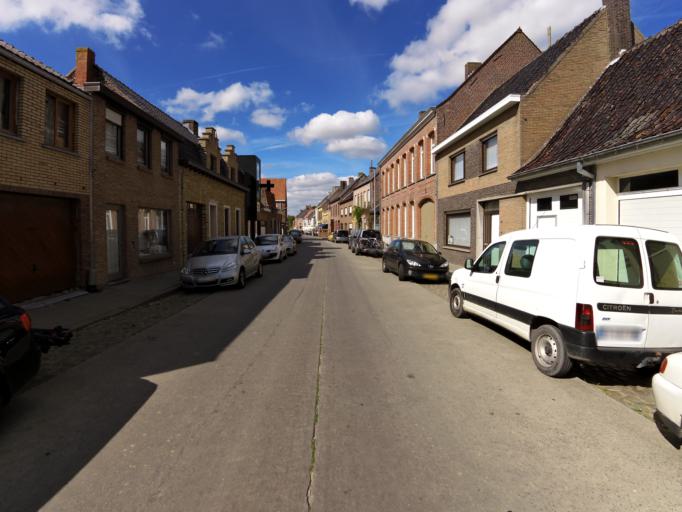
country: FR
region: Nord-Pas-de-Calais
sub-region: Departement du Nord
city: Steenvoorde
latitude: 50.8577
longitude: 2.6205
